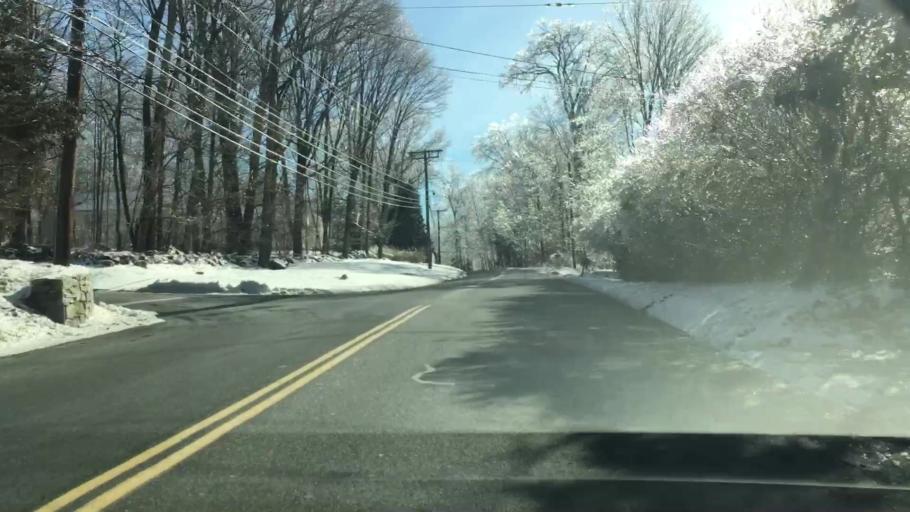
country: US
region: Connecticut
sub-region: Fairfield County
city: Trumbull
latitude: 41.3375
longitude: -73.2250
